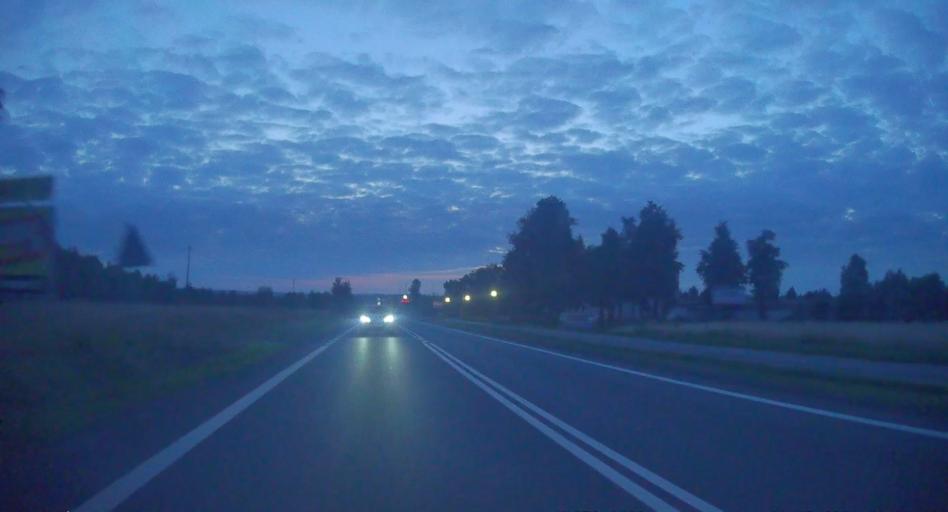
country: PL
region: Silesian Voivodeship
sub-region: Powiat klobucki
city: Klobuck
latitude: 50.8972
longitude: 18.9475
